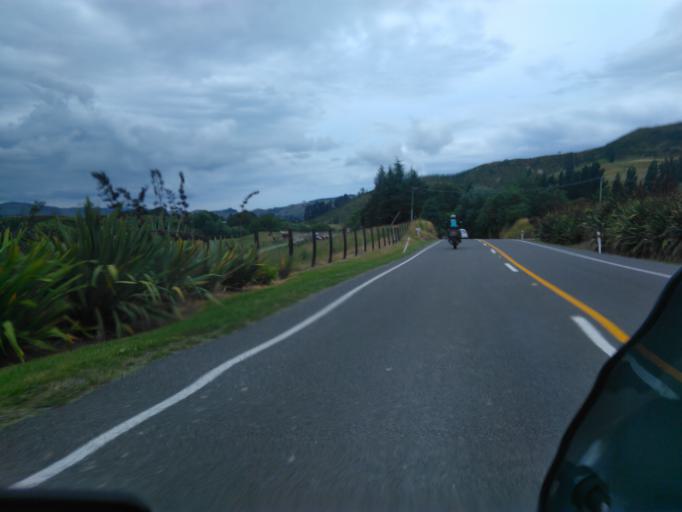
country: NZ
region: Gisborne
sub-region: Gisborne District
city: Gisborne
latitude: -38.4647
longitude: 177.8116
